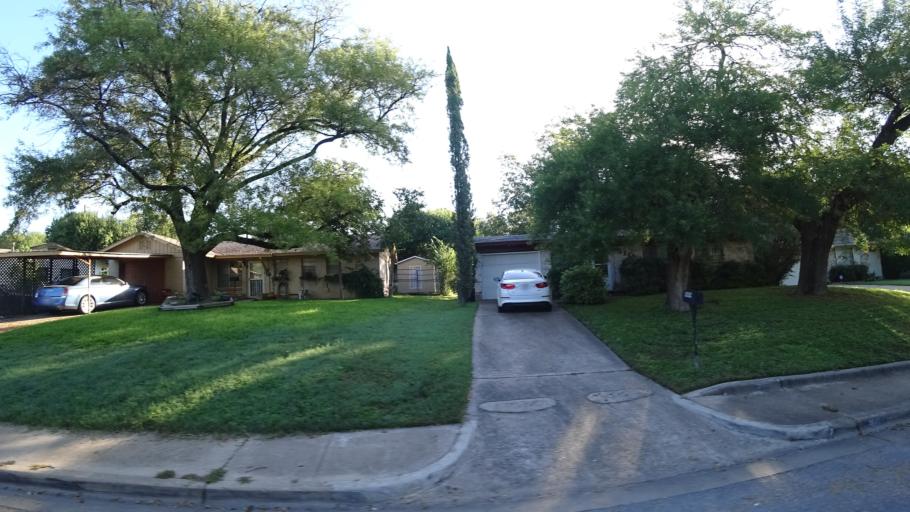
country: US
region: Texas
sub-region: Travis County
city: Wells Branch
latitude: 30.3588
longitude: -97.6971
